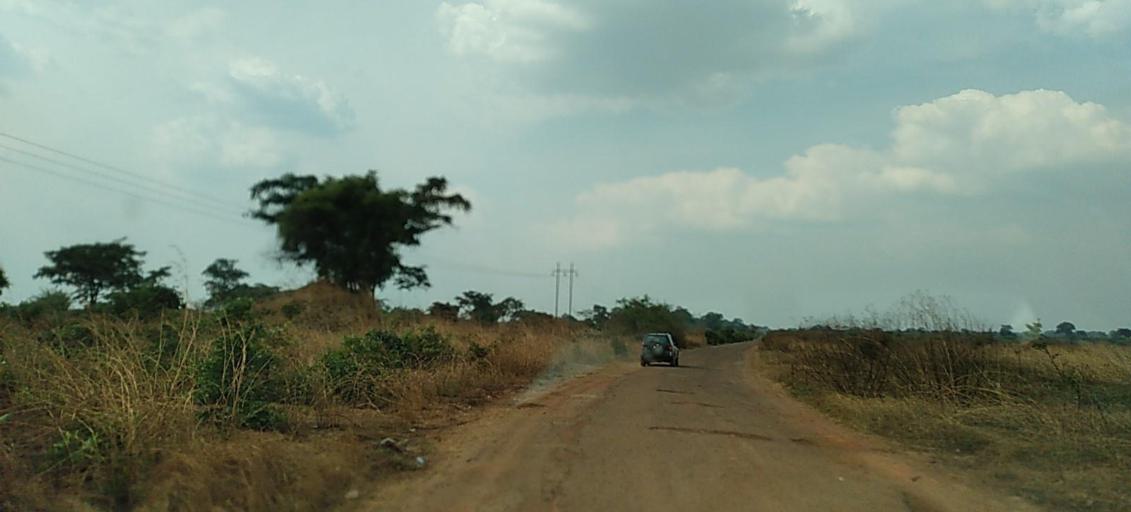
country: ZM
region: Copperbelt
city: Chililabombwe
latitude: -12.3931
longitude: 27.8062
